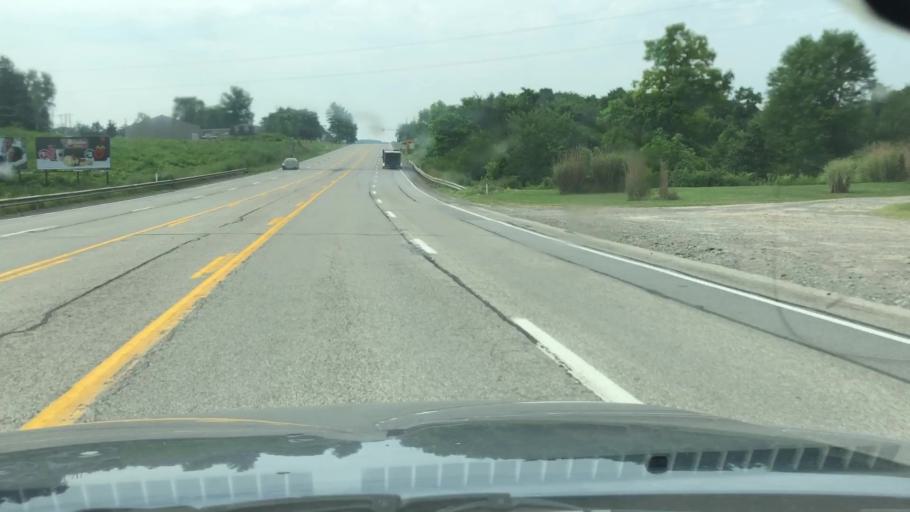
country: US
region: Pennsylvania
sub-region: Butler County
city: Nixon
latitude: 40.7339
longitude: -79.9243
